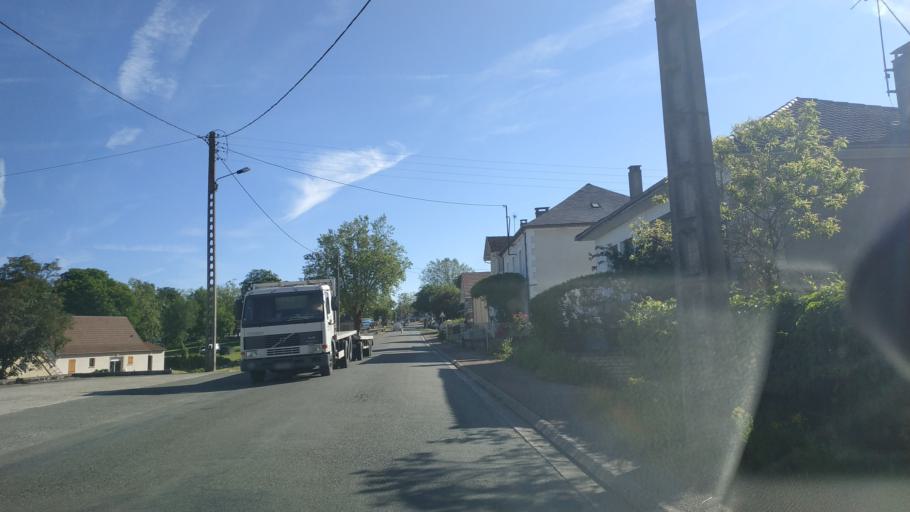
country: FR
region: Midi-Pyrenees
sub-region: Departement du Lot
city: Lacapelle-Marival
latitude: 44.6739
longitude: 1.8734
